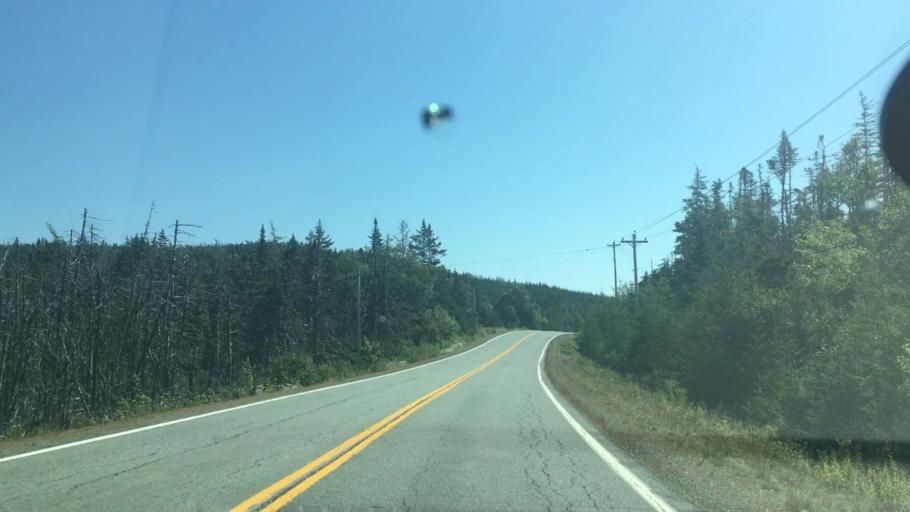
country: CA
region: Nova Scotia
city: Antigonish
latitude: 45.0122
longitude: -62.0936
